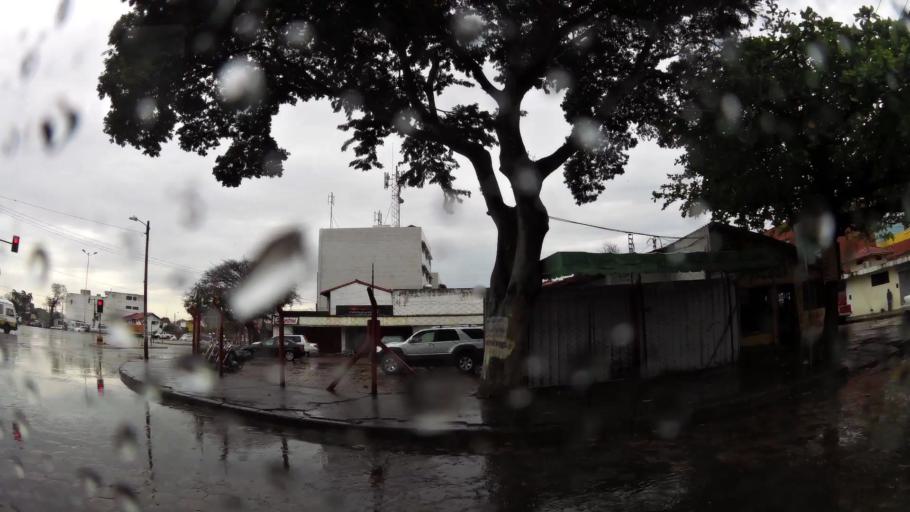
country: BO
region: Santa Cruz
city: Santa Cruz de la Sierra
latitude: -17.7987
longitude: -63.1753
